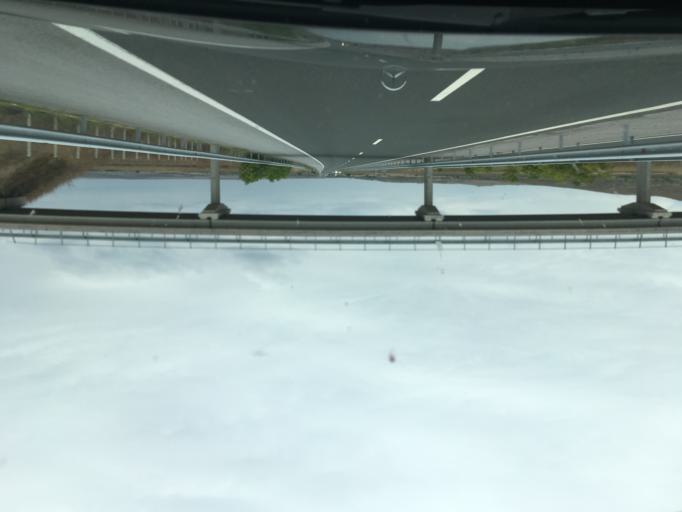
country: BG
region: Sliven
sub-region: Obshtina Sliven
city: Kermen
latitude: 42.5046
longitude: 26.3127
